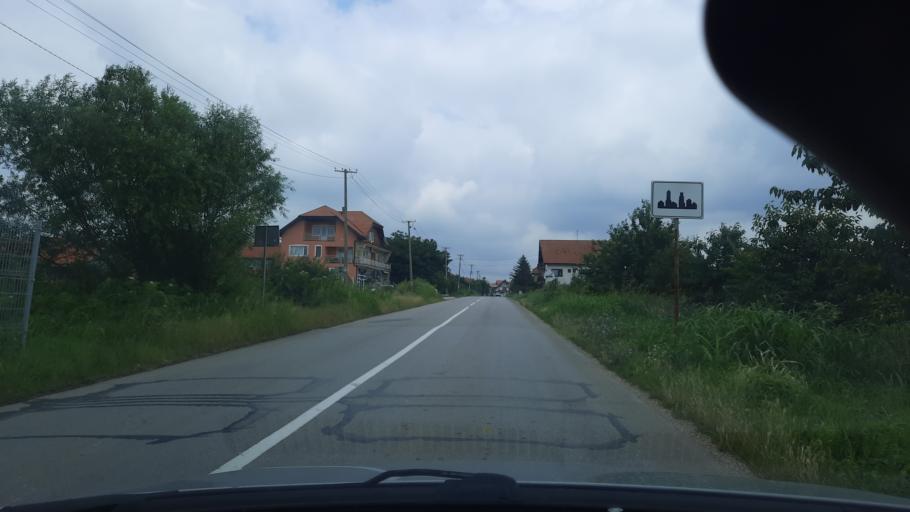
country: RS
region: Central Serbia
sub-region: Branicevski Okrug
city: Malo Crnice
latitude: 44.5734
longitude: 21.3579
